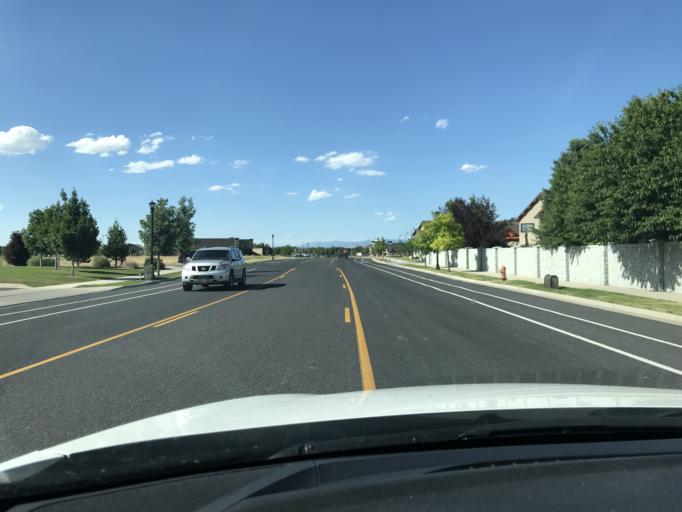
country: US
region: Utah
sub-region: Salt Lake County
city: South Jordan Heights
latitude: 40.5582
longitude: -111.9727
